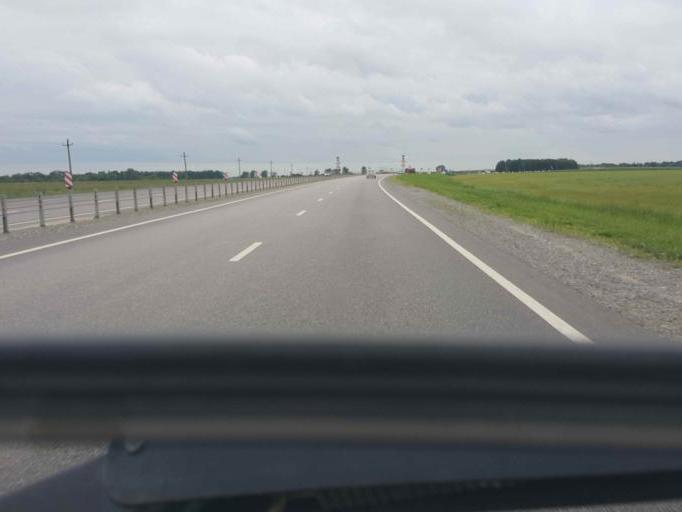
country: RU
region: Tambov
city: Zavoronezhskoye
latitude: 52.9050
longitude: 40.6458
